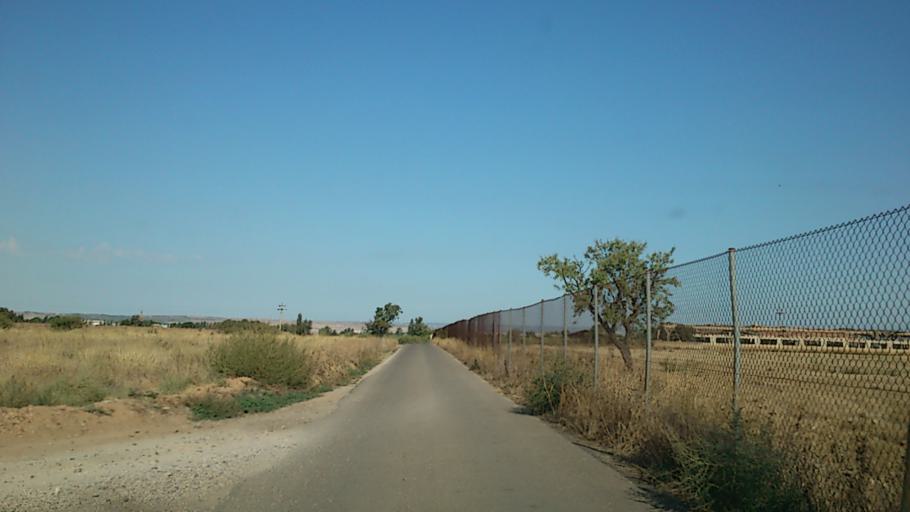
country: ES
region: Aragon
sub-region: Provincia de Zaragoza
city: Villanueva de Gallego
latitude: 41.7256
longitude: -0.7993
